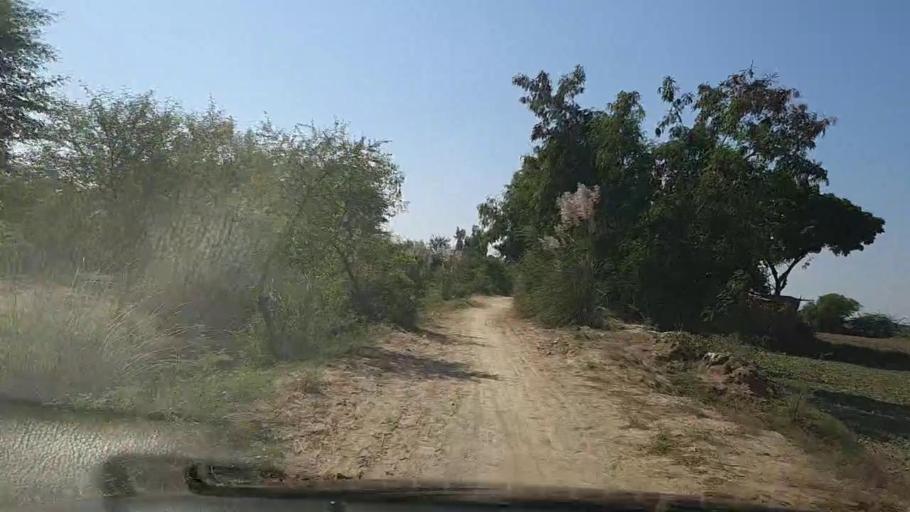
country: PK
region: Sindh
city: Mirpur Sakro
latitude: 24.5868
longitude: 67.8141
